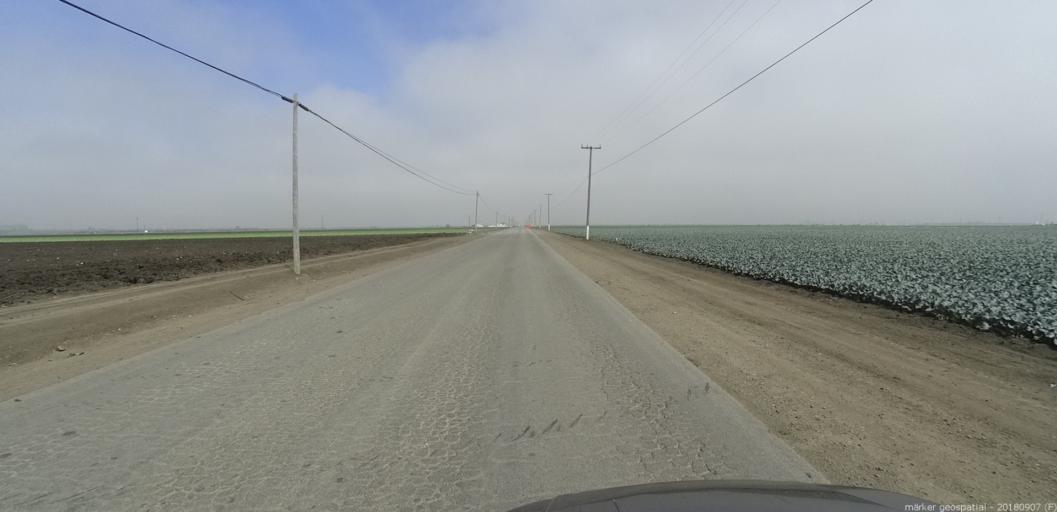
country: US
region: California
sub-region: Monterey County
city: Castroville
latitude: 36.7073
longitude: -121.7374
